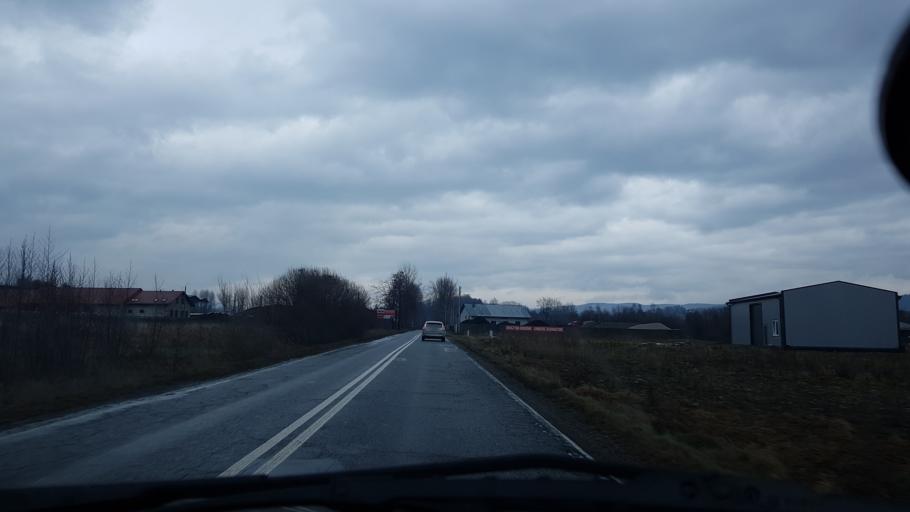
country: PL
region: Silesian Voivodeship
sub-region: Powiat zywiecki
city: Lekawica
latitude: 49.7114
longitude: 19.2471
